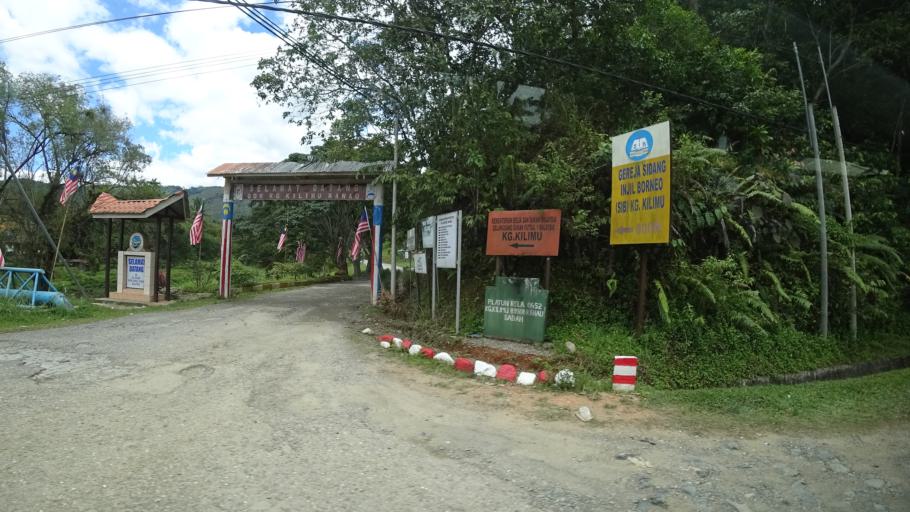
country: MY
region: Sabah
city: Ranau
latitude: 5.9780
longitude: 116.6823
